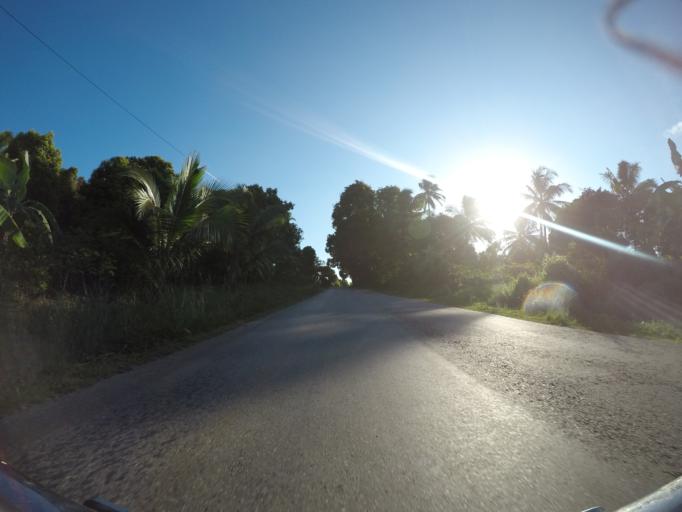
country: TZ
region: Pemba South
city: Mtambile
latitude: -5.3728
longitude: 39.7057
